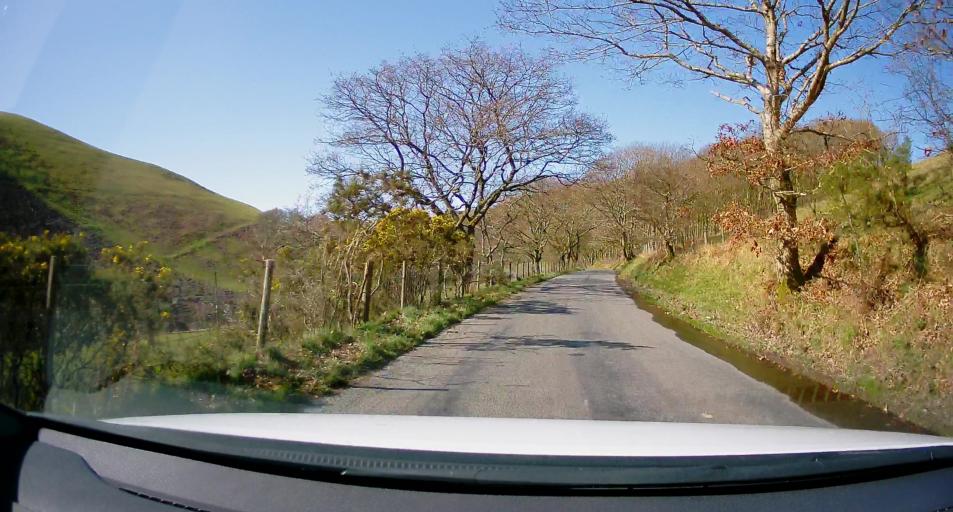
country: GB
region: Wales
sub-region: County of Ceredigion
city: Lledrod
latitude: 52.3521
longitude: -3.9133
